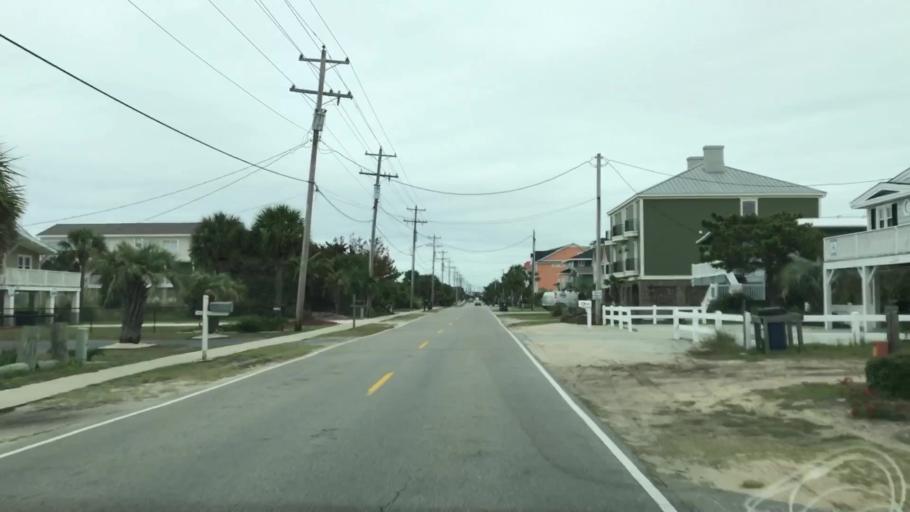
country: US
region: South Carolina
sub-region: Georgetown County
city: Murrells Inlet
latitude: 33.5588
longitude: -79.0140
